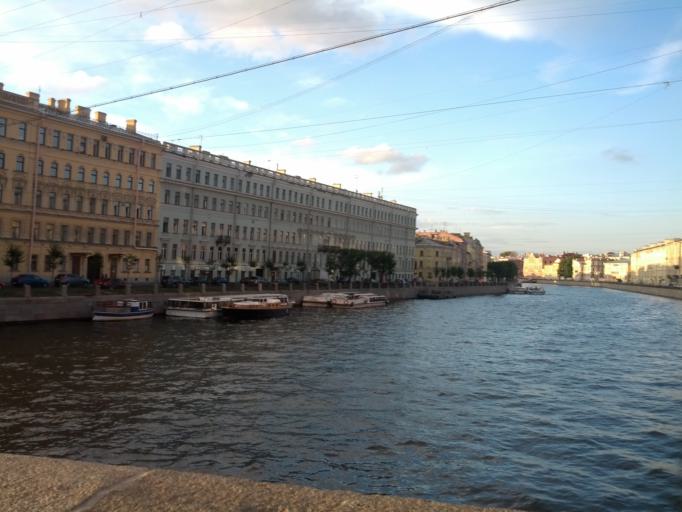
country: RU
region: St.-Petersburg
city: Centralniy
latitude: 59.9284
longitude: 30.3364
